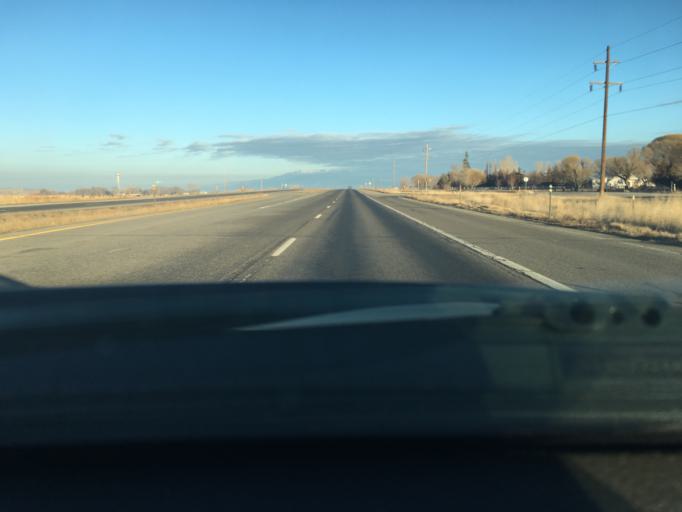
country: US
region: Colorado
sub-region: Montrose County
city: Olathe
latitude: 38.5564
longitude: -107.9519
